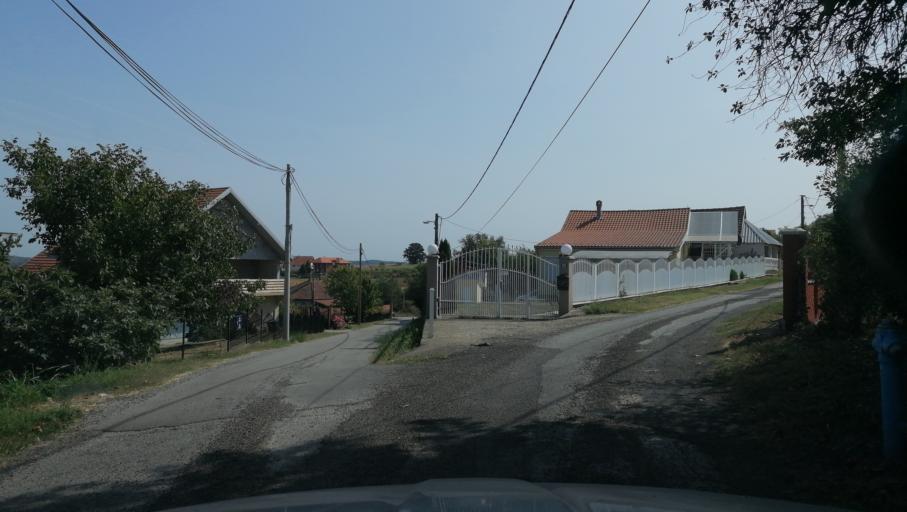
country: RS
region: Central Serbia
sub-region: Belgrade
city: Zvezdara
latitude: 44.6915
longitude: 20.5545
